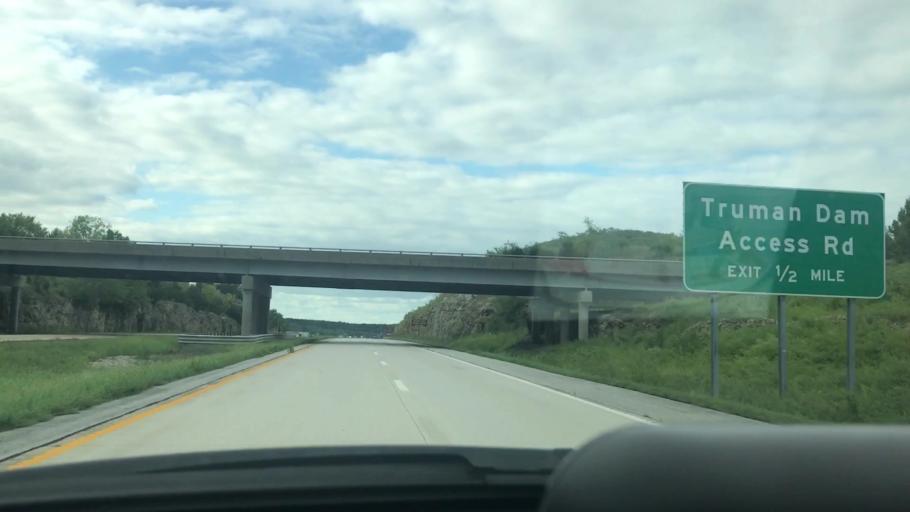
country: US
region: Missouri
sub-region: Benton County
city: Warsaw
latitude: 38.2530
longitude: -93.3637
